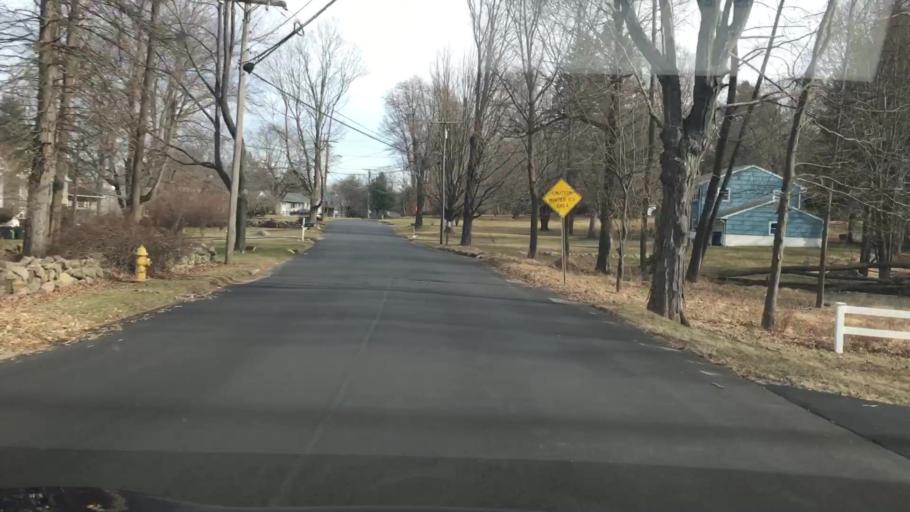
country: US
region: New York
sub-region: Putnam County
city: Peach Lake
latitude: 41.3781
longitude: -73.5224
